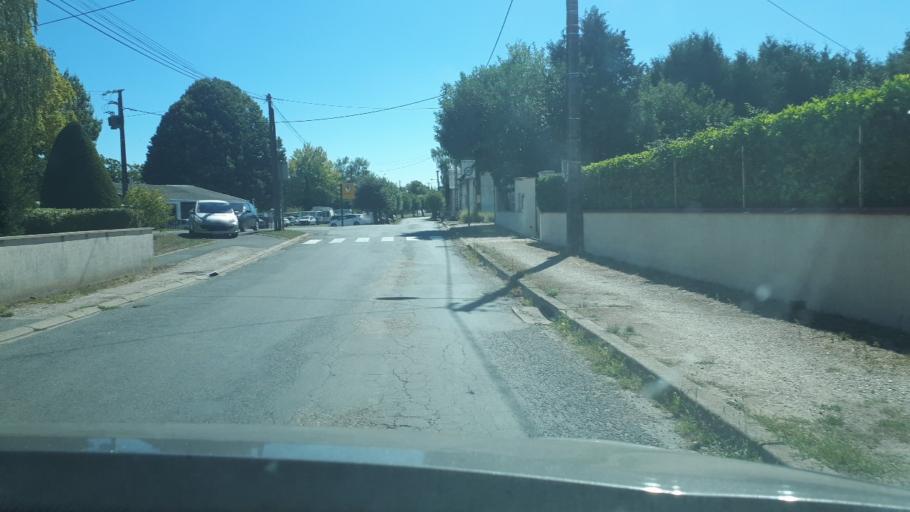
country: FR
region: Centre
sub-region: Departement du Cher
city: Sancerre
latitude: 47.2541
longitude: 2.7595
